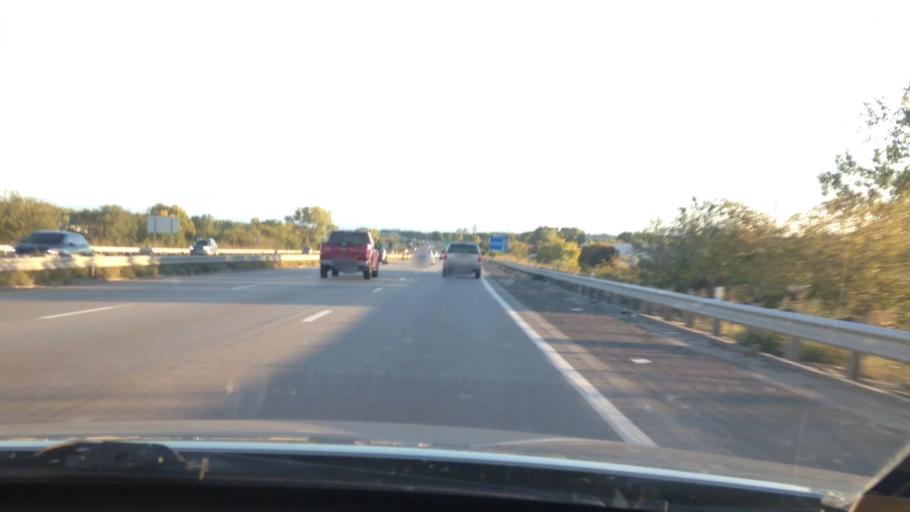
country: US
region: Missouri
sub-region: Clay County
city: Claycomo
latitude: 39.1447
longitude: -94.4987
